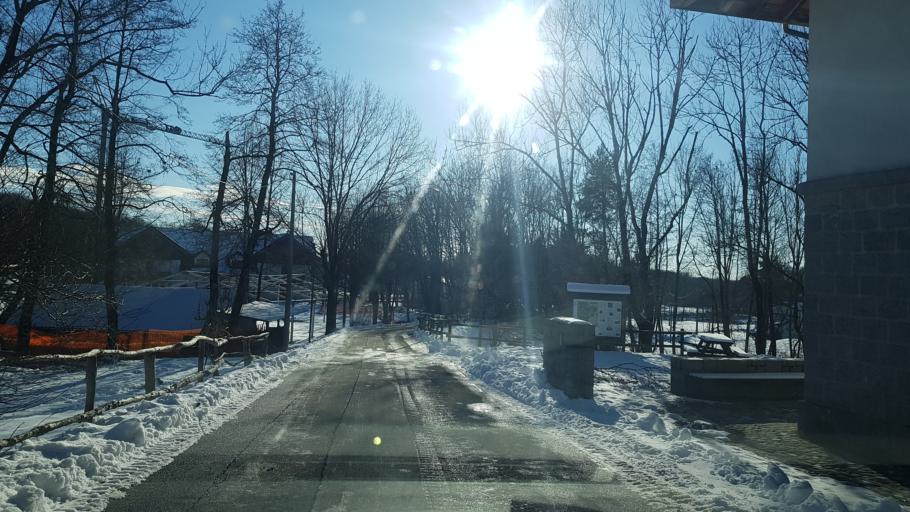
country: IT
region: Friuli Venezia Giulia
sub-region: Provincia di Udine
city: Forgaria nel Friuli
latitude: 46.2461
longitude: 12.9911
